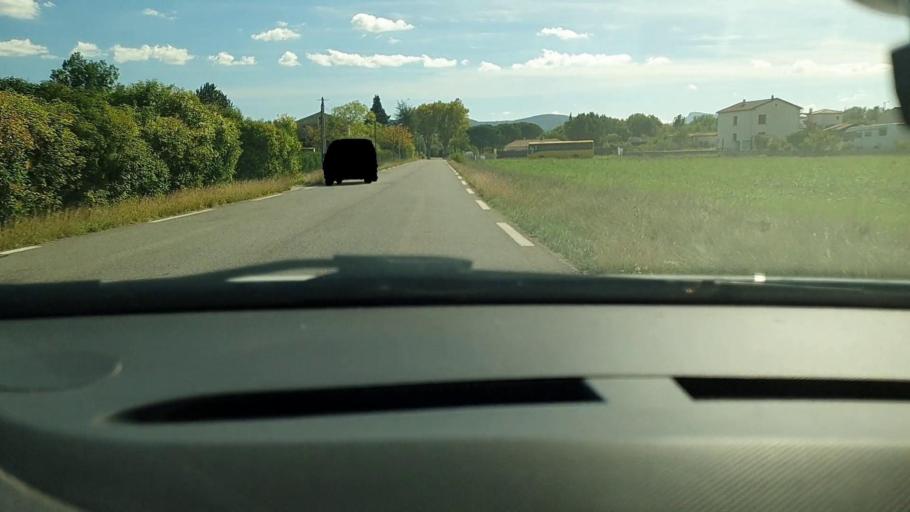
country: FR
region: Languedoc-Roussillon
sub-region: Departement du Gard
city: Saint-Ambroix
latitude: 44.2374
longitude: 4.2428
